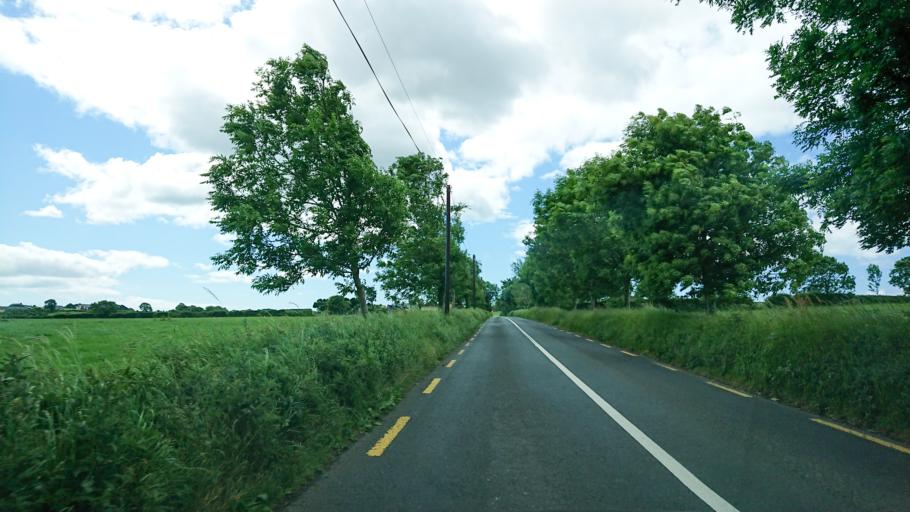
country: IE
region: Munster
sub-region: Waterford
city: Tra Mhor
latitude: 52.2189
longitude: -7.1978
